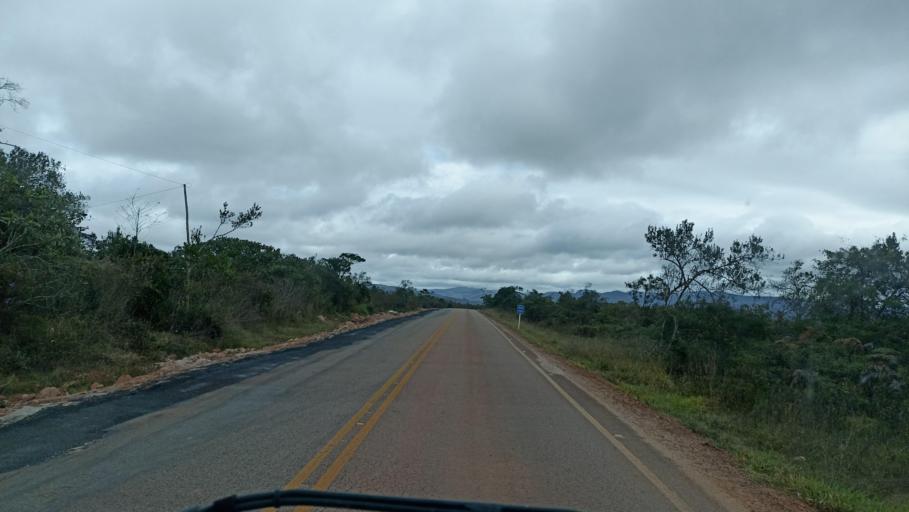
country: BR
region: Bahia
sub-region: Andarai
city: Vera Cruz
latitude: -12.9581
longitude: -41.3208
